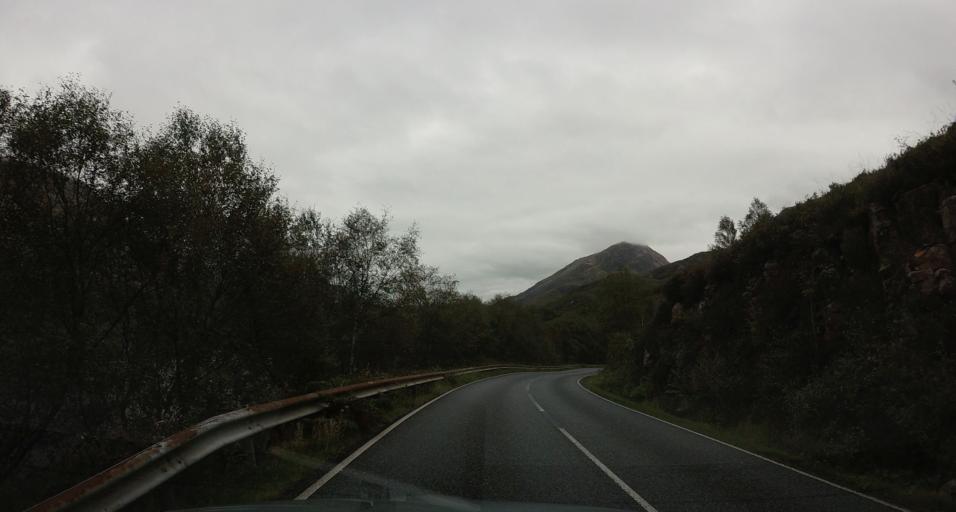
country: GB
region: Scotland
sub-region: Highland
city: Fort William
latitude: 56.6988
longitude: -5.0659
